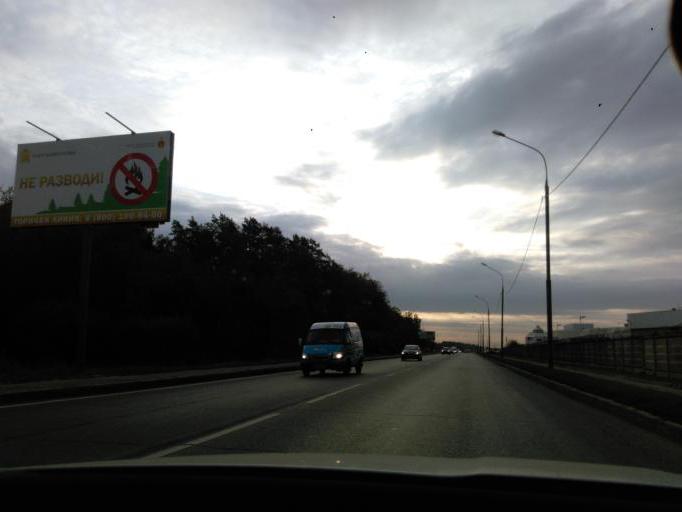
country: RU
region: Moskovskaya
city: Lobnya
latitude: 55.9844
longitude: 37.4333
